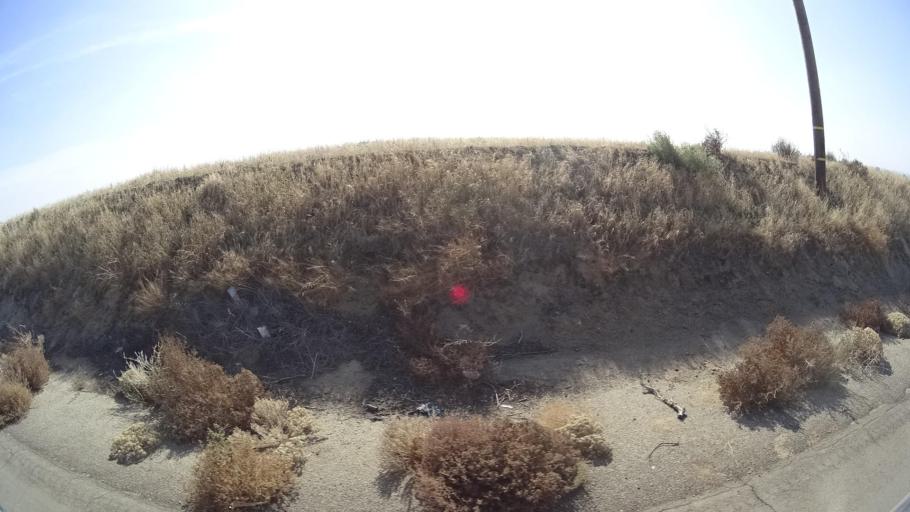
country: US
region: California
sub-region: Kern County
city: Oildale
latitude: 35.5299
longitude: -119.0978
